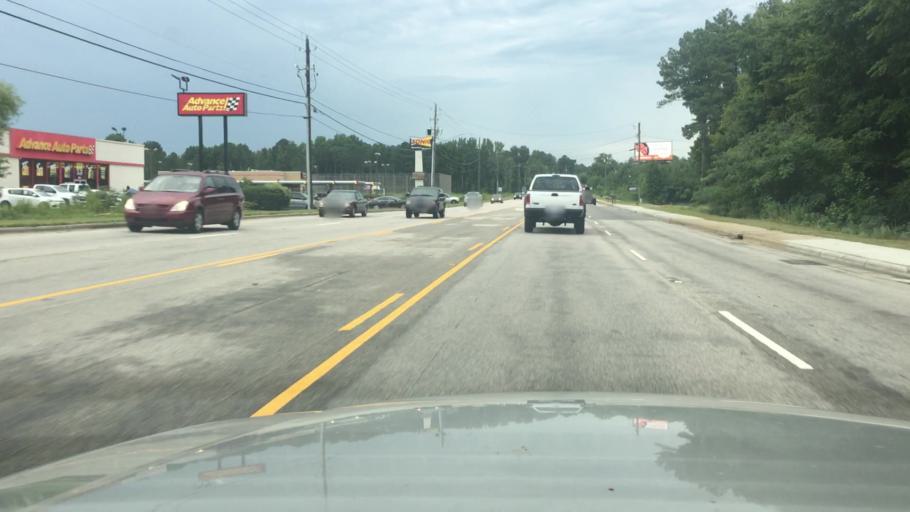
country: US
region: North Carolina
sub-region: Cumberland County
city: Hope Mills
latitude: 34.9888
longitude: -78.9662
